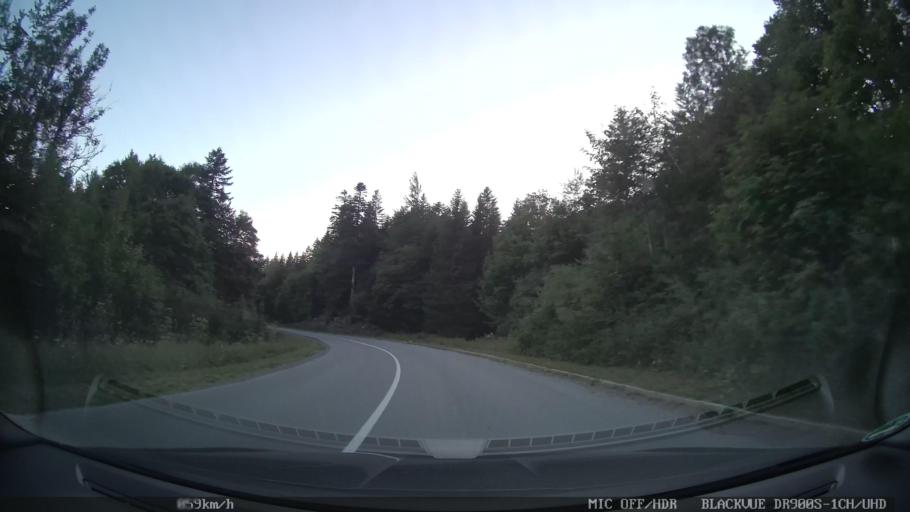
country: HR
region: Primorsko-Goranska
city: Novi Vinodolski
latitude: 45.1707
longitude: 14.9658
